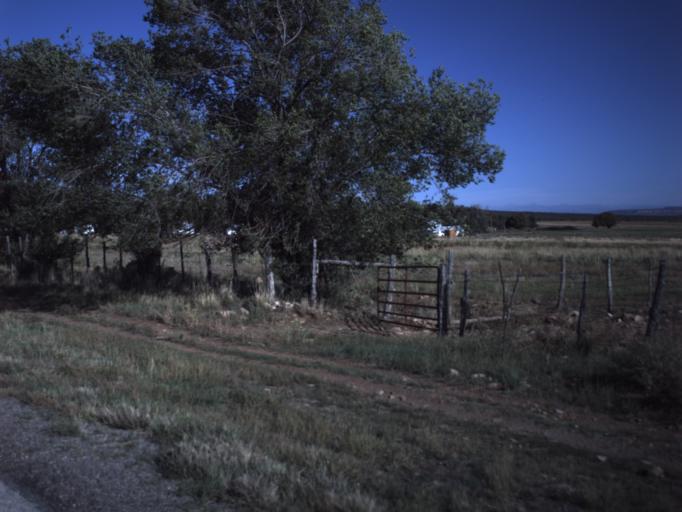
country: US
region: Utah
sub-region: Grand County
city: Moab
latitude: 38.3119
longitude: -109.2544
